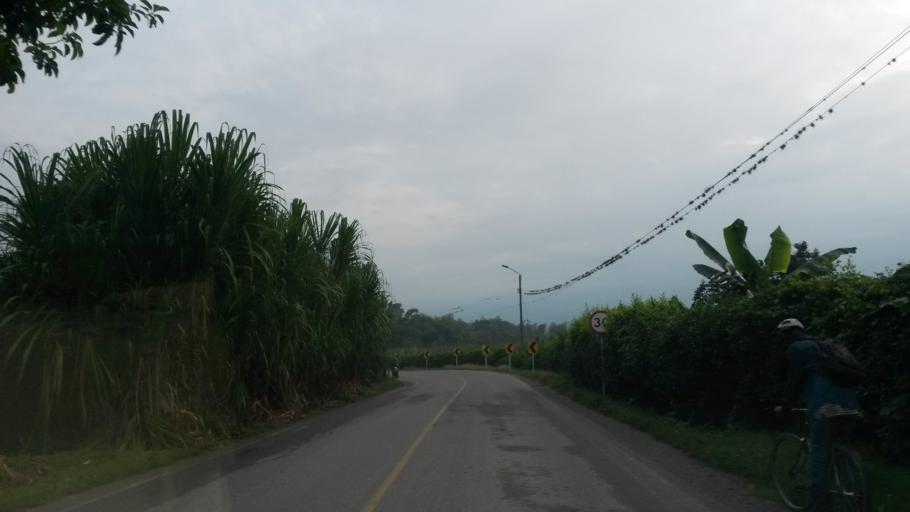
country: CO
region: Cauca
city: Padilla
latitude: 3.2277
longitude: -76.3174
